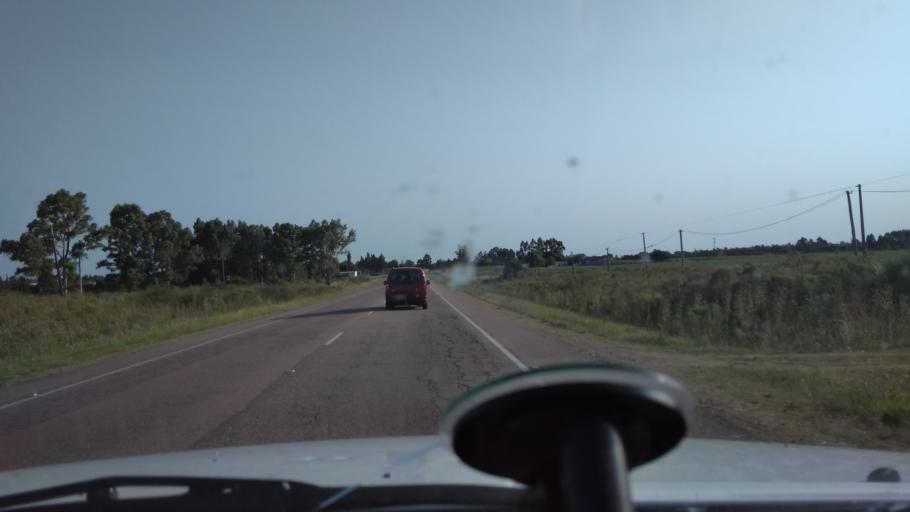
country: UY
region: Canelones
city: Sauce
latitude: -34.6332
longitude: -56.0519
